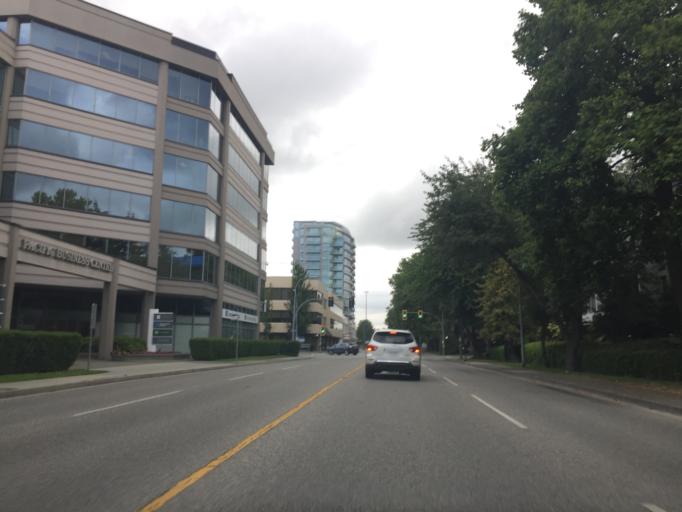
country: CA
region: British Columbia
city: Richmond
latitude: 49.1711
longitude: -123.1314
